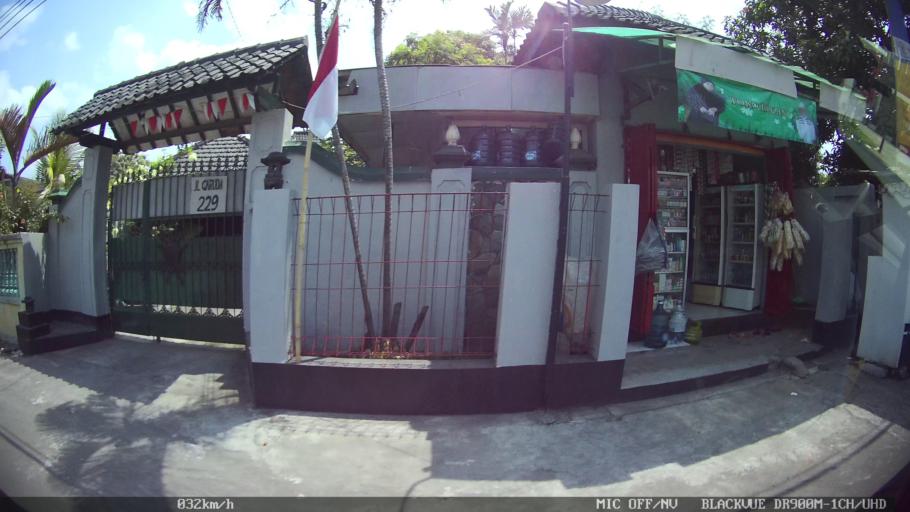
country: ID
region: Daerah Istimewa Yogyakarta
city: Depok
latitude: -7.8149
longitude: 110.4084
